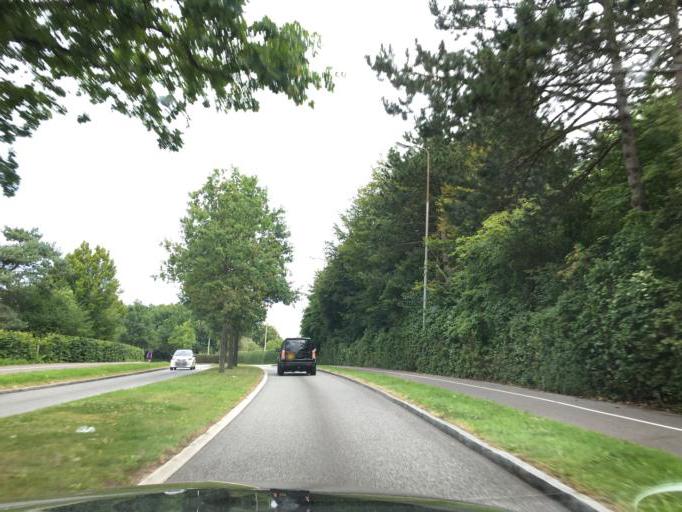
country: DK
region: Capital Region
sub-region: Horsholm Kommune
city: Horsholm
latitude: 55.8940
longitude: 12.4995
